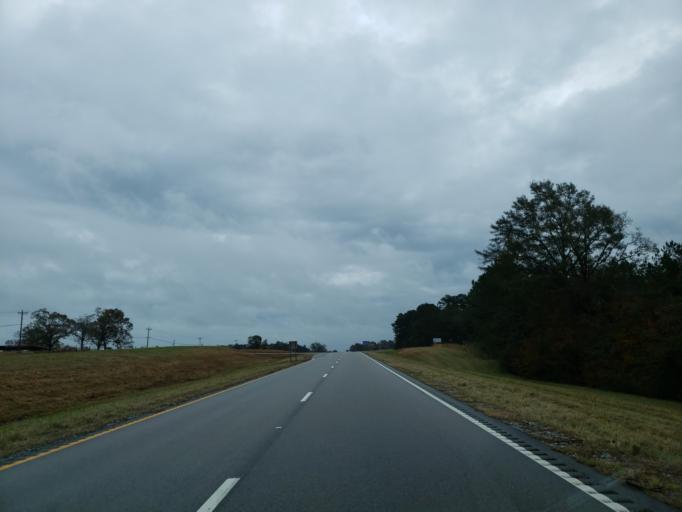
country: US
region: Mississippi
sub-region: Wayne County
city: Waynesboro
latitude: 31.6956
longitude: -88.7371
